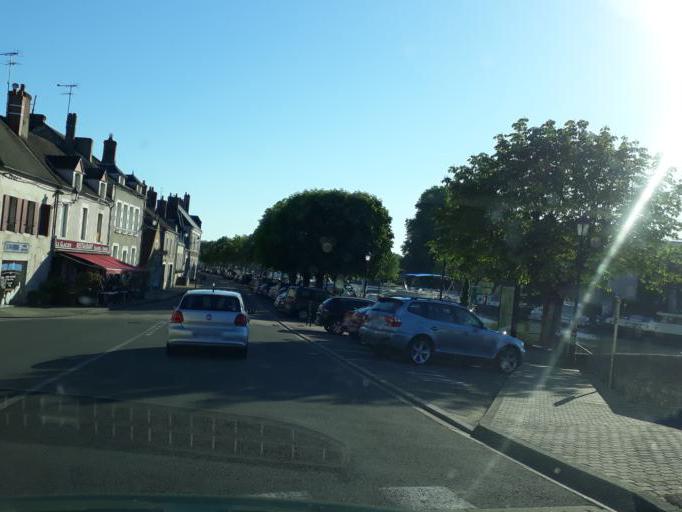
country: FR
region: Centre
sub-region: Departement du Loiret
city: Briare
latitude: 47.6398
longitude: 2.7375
